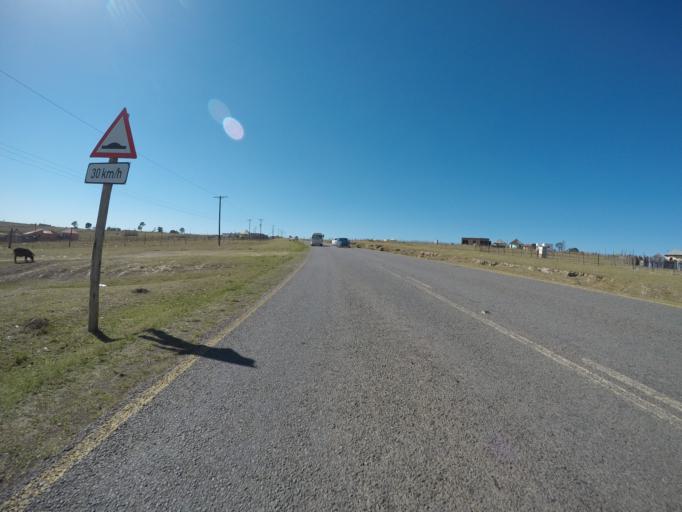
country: ZA
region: Eastern Cape
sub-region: OR Tambo District Municipality
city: Mthatha
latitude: -31.8825
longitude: 28.7563
